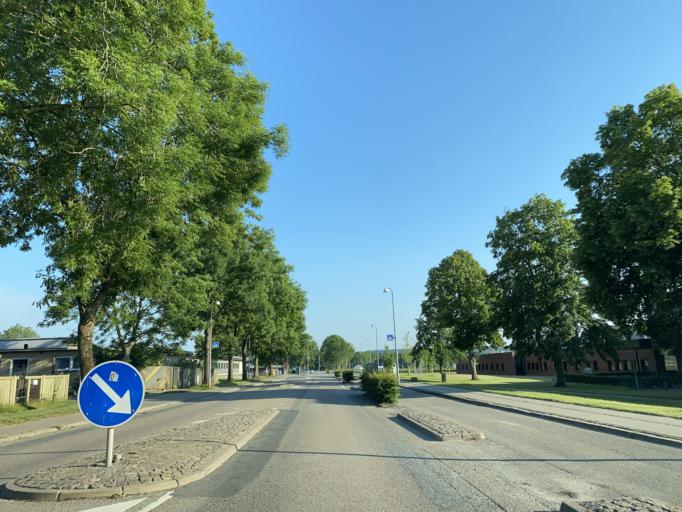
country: DK
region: South Denmark
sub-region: Aabenraa Kommune
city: Aabenraa
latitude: 55.0438
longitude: 9.4131
